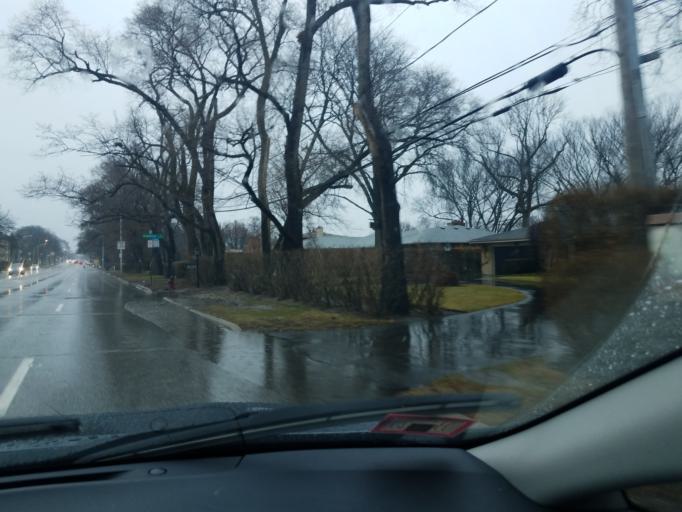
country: US
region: Illinois
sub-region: Cook County
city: Skokie
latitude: 42.0368
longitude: -87.7471
